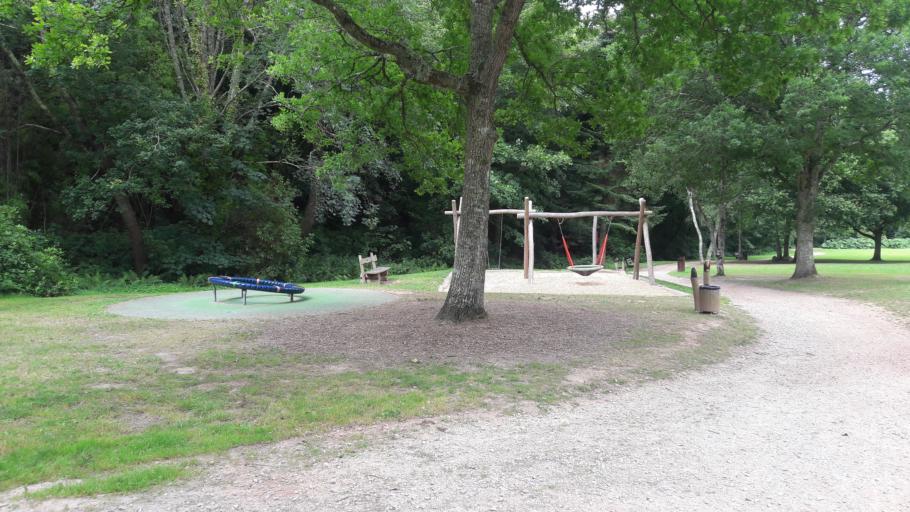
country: FR
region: Lower Normandy
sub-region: Departement de la Manche
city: Tourlaville
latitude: 49.6288
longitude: -1.5617
